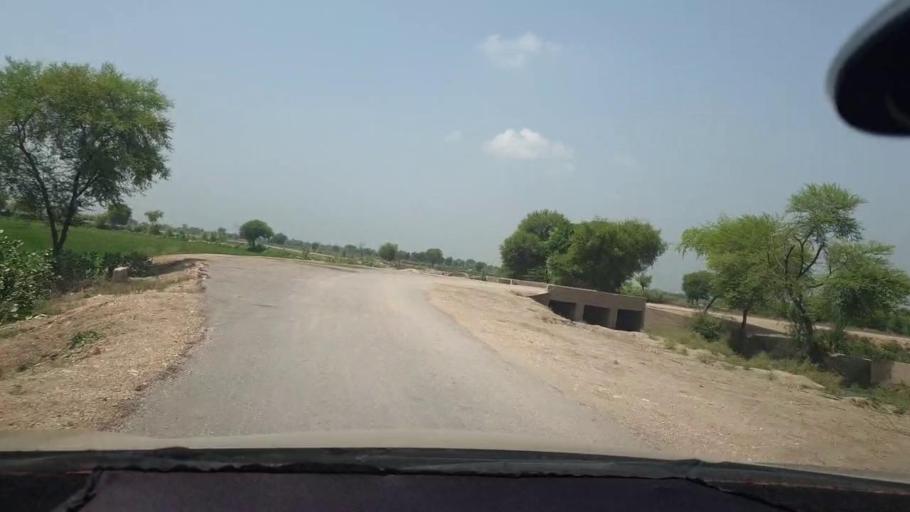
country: PK
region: Sindh
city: Kambar
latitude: 27.6640
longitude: 67.9158
